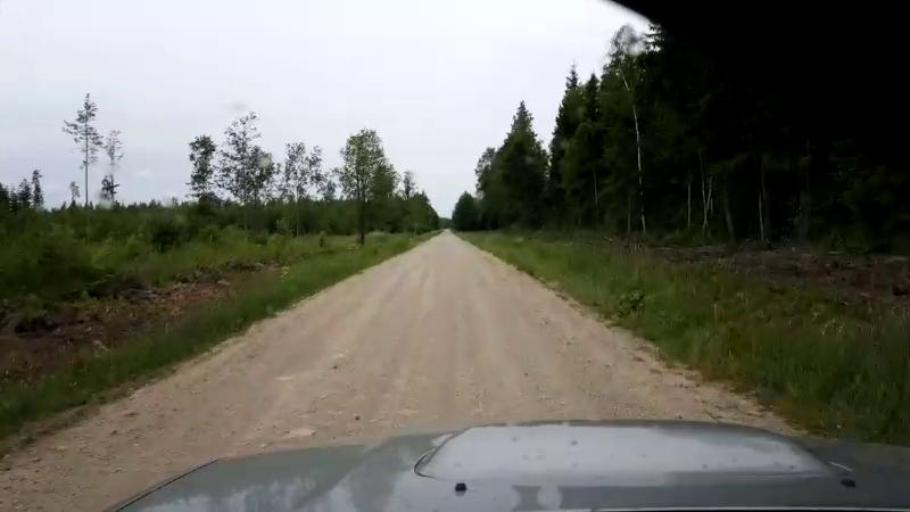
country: EE
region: Paernumaa
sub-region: Halinga vald
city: Parnu-Jaagupi
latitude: 58.5383
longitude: 24.5955
